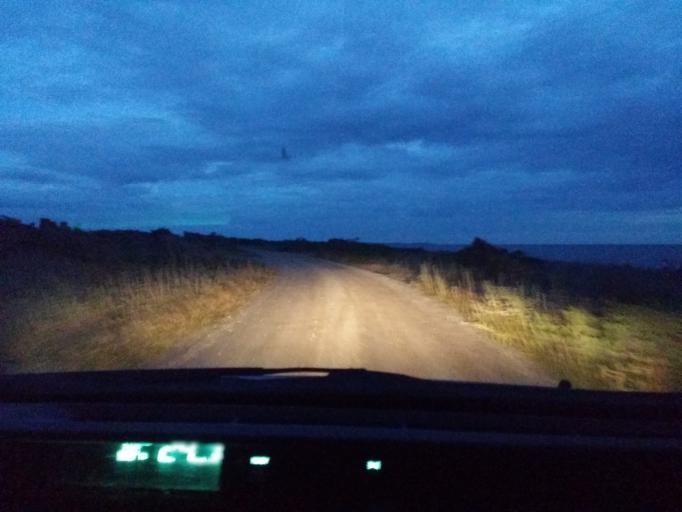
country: SE
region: Kalmar
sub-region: Borgholms Kommun
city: Borgholm
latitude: 57.1406
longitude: 16.9065
